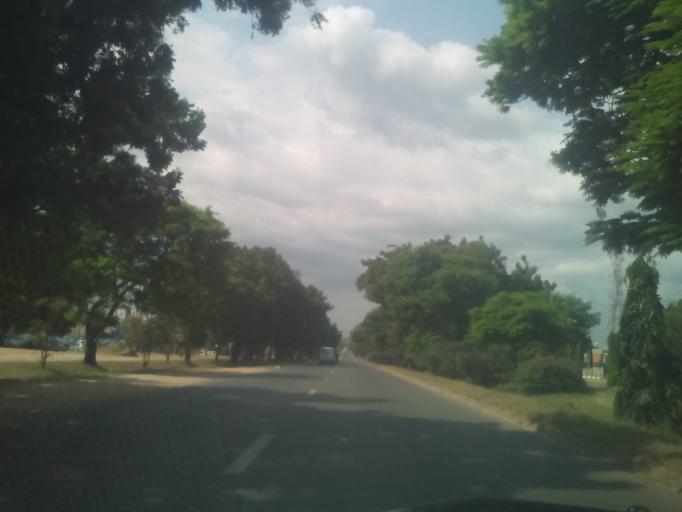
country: TZ
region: Dar es Salaam
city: Dar es Salaam
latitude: -6.8408
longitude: 39.2522
